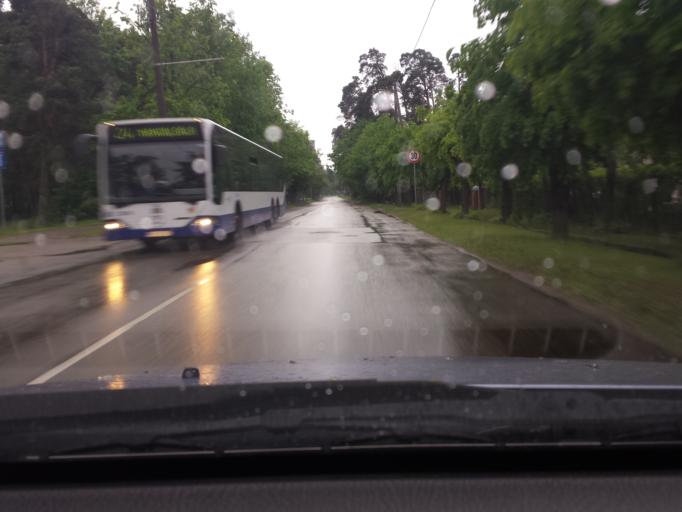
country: LV
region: Riga
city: Bolderaja
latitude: 57.0462
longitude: 24.0934
